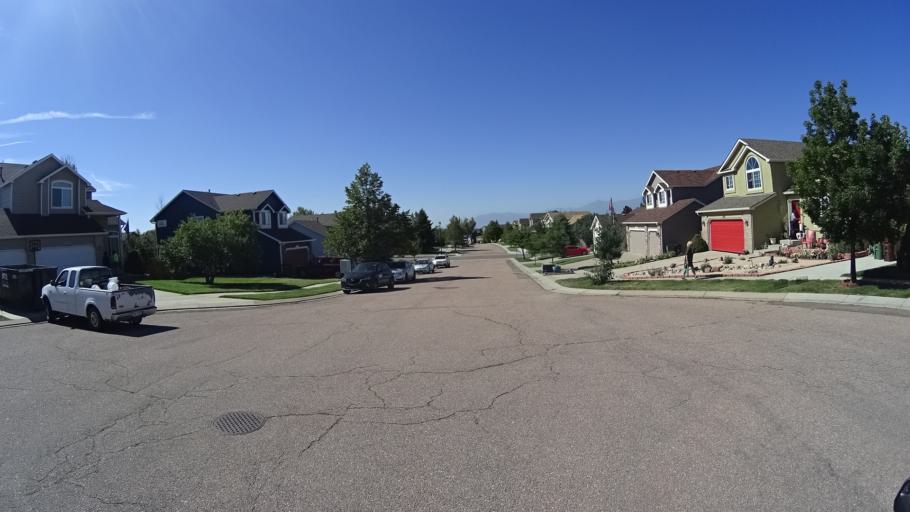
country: US
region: Colorado
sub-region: El Paso County
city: Black Forest
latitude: 38.9537
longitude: -104.7253
